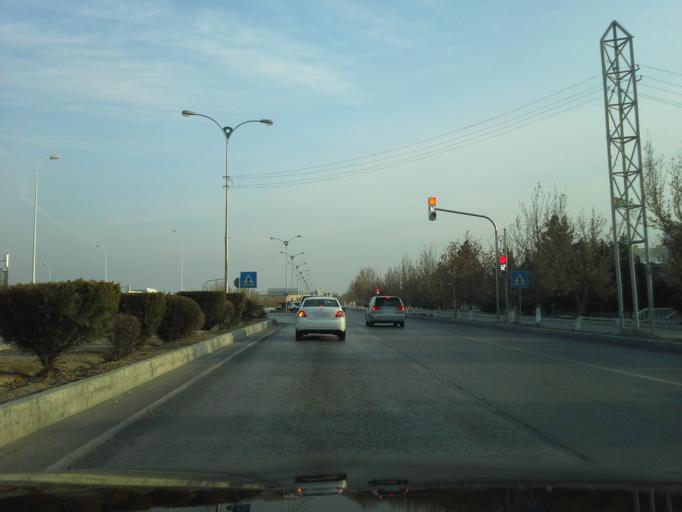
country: TM
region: Ahal
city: Abadan
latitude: 38.0522
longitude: 58.1840
